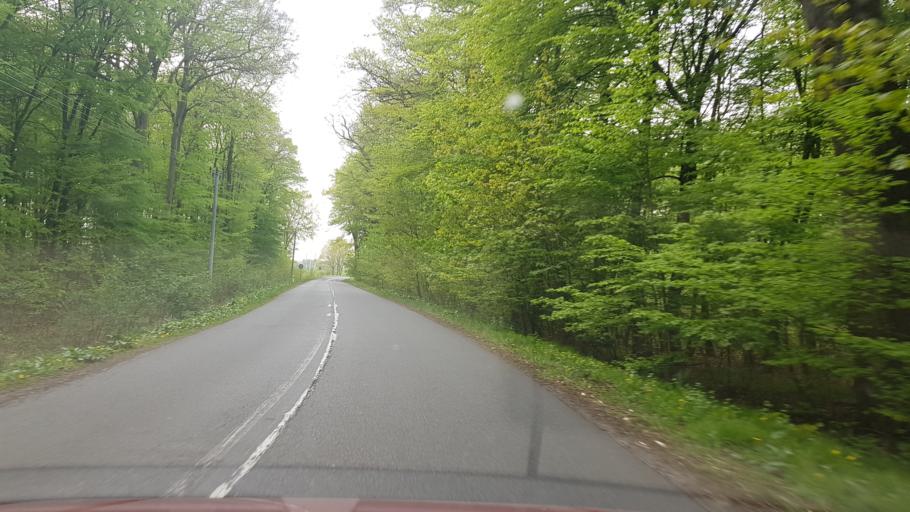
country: PL
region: West Pomeranian Voivodeship
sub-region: Powiat gryfinski
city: Stare Czarnowo
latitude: 53.2868
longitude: 14.7429
